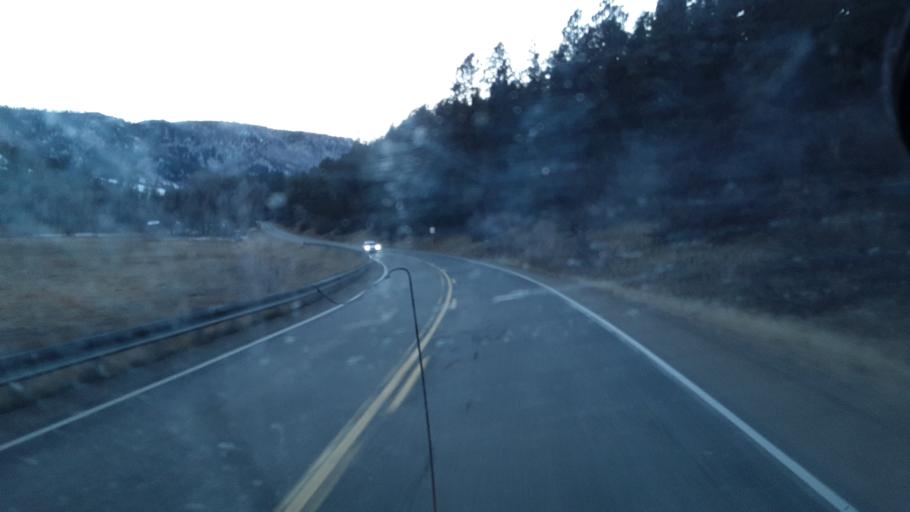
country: US
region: Colorado
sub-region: La Plata County
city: Bayfield
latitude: 37.3429
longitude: -107.7203
